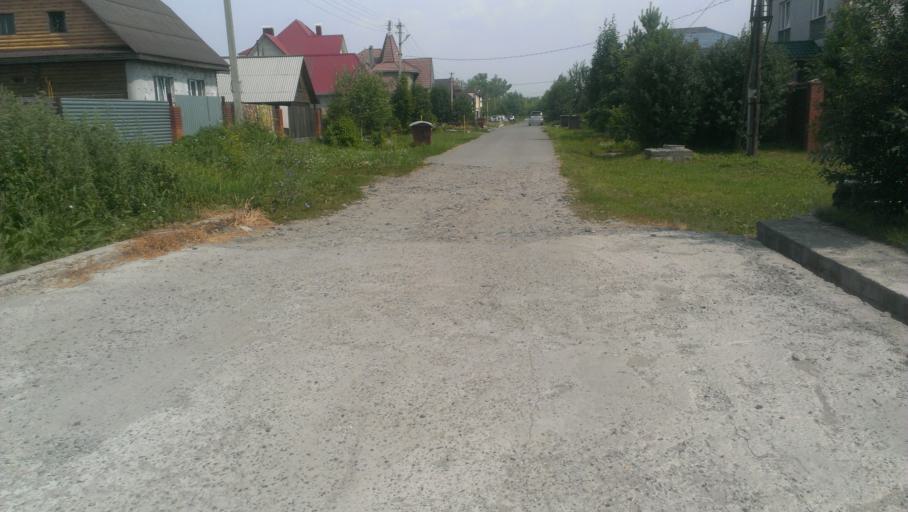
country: RU
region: Altai Krai
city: Novosilikatnyy
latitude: 53.3490
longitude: 83.6424
